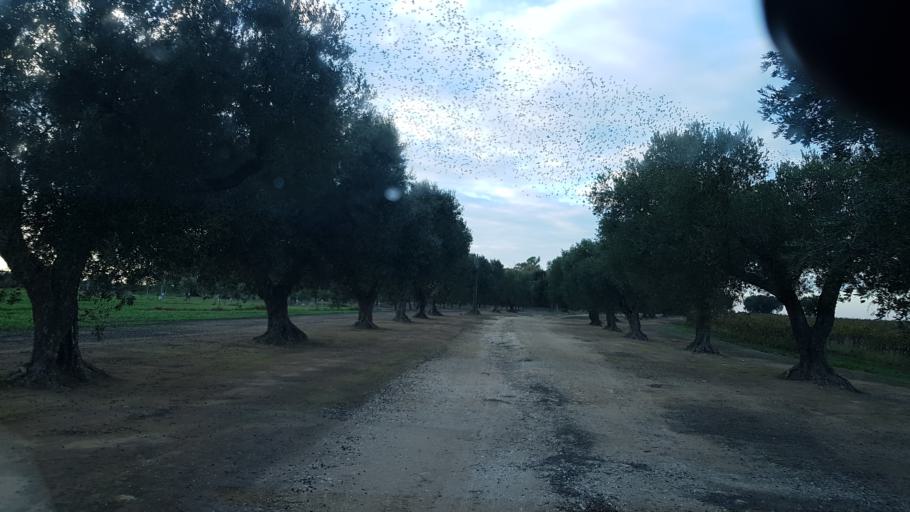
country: IT
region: Apulia
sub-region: Provincia di Brindisi
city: La Rosa
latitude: 40.5876
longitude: 17.9921
